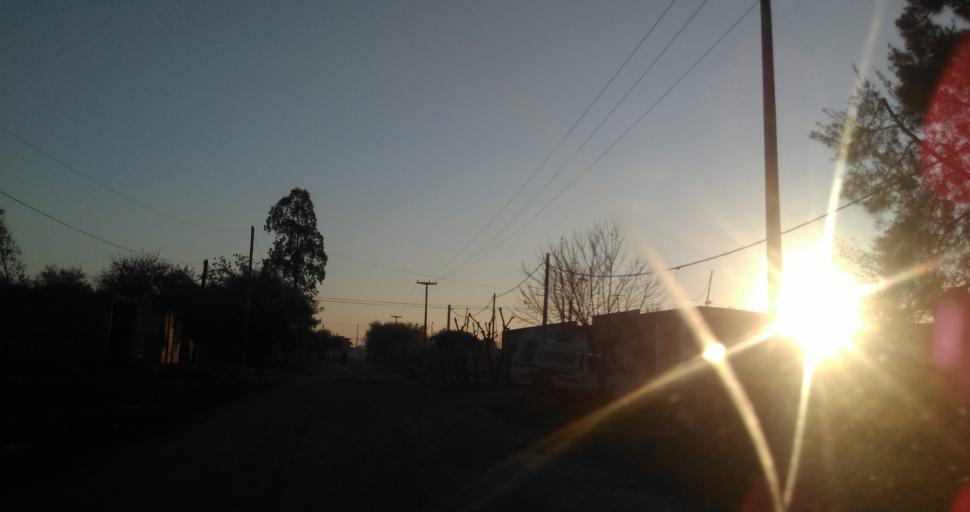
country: AR
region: Chaco
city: Resistencia
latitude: -27.4812
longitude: -59.0040
